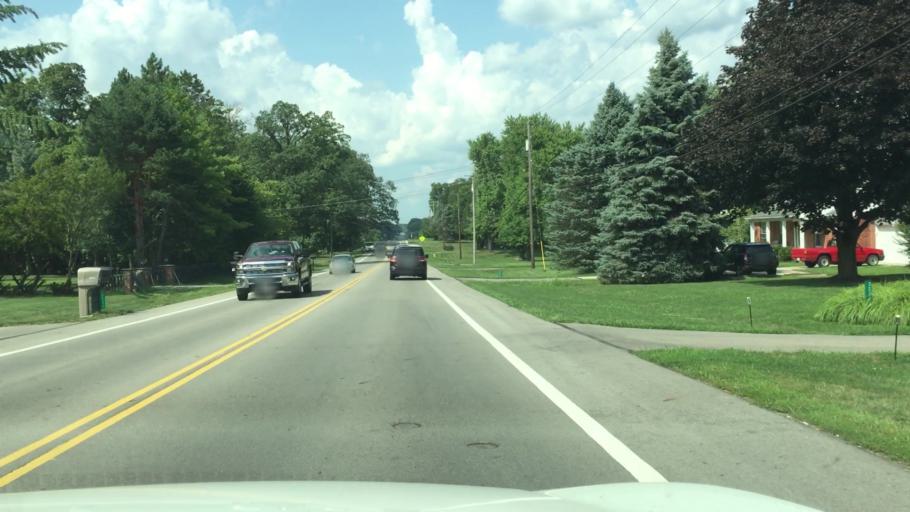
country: US
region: Ohio
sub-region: Clark County
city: Northridge
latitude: 39.9704
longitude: -83.7847
